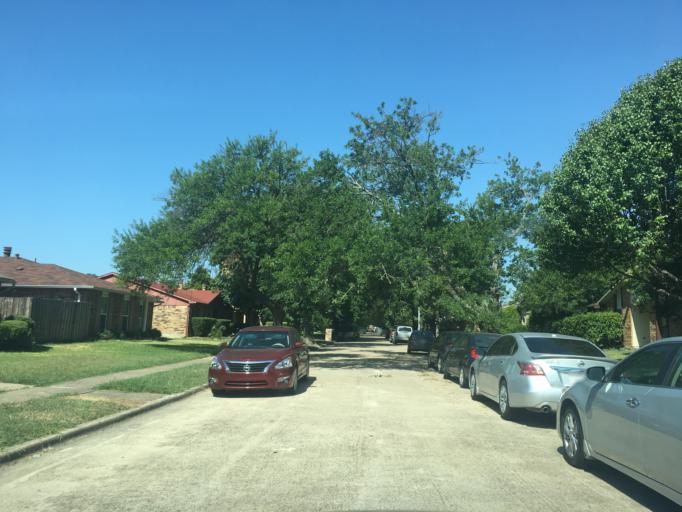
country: US
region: Texas
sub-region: Dallas County
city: Garland
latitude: 32.8548
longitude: -96.6609
